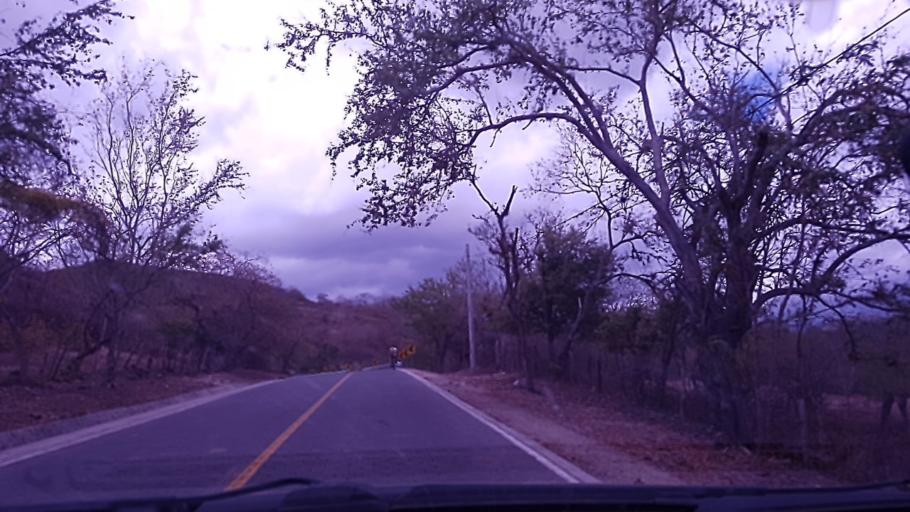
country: NI
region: Esteli
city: Condega
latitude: 13.3726
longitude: -86.3844
